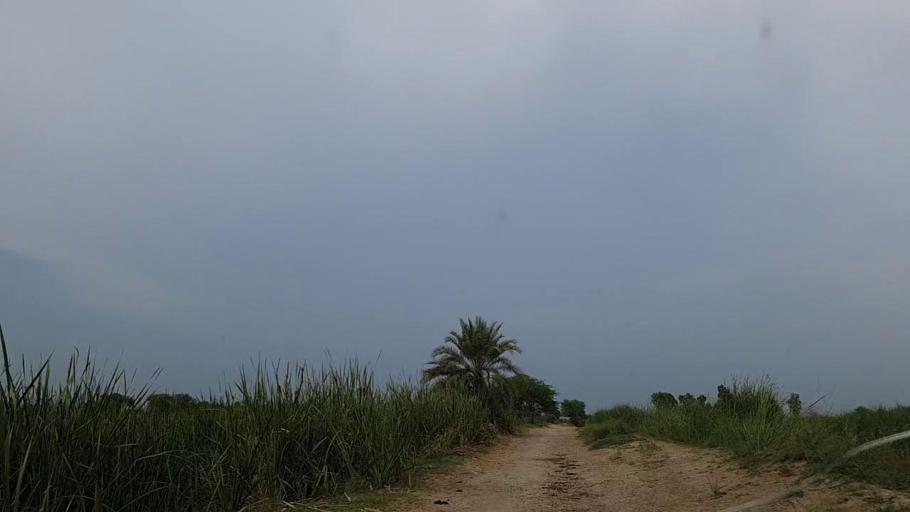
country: PK
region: Sindh
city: Khanpur
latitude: 27.8176
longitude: 69.5348
